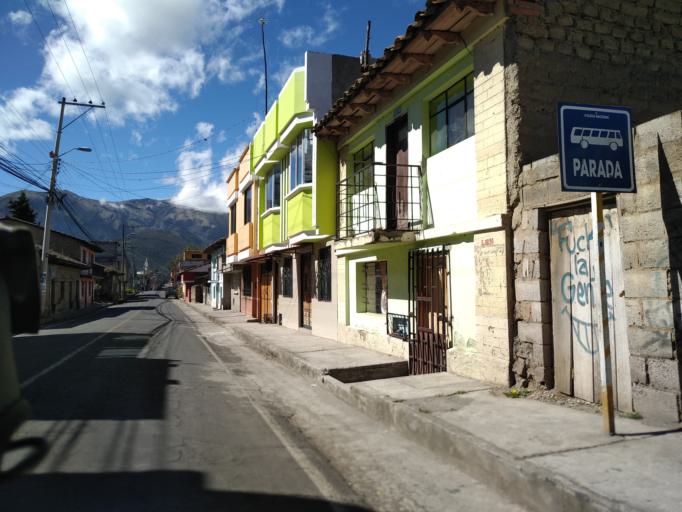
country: EC
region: Imbabura
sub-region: Canton Otavalo
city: Otavalo
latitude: 0.2076
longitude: -78.2024
